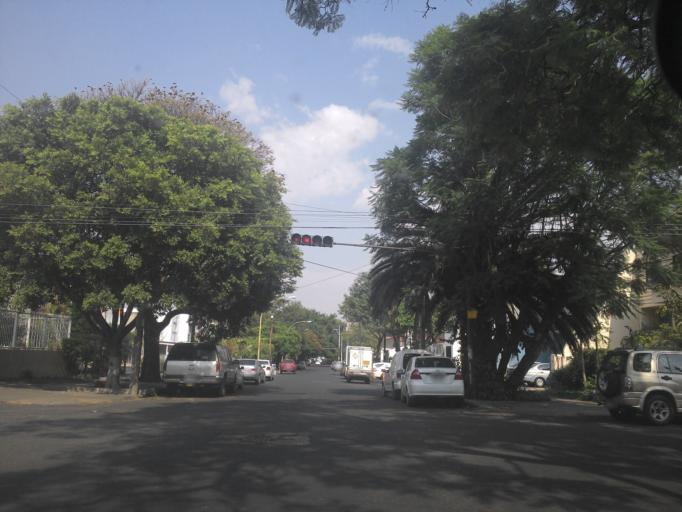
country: MX
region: Jalisco
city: Guadalajara
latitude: 20.6653
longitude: -103.3655
